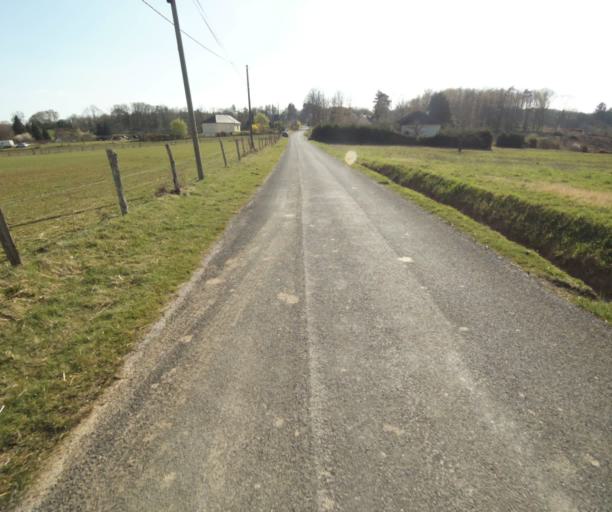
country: FR
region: Limousin
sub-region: Departement de la Correze
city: Saint-Mexant
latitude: 45.3204
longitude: 1.6237
